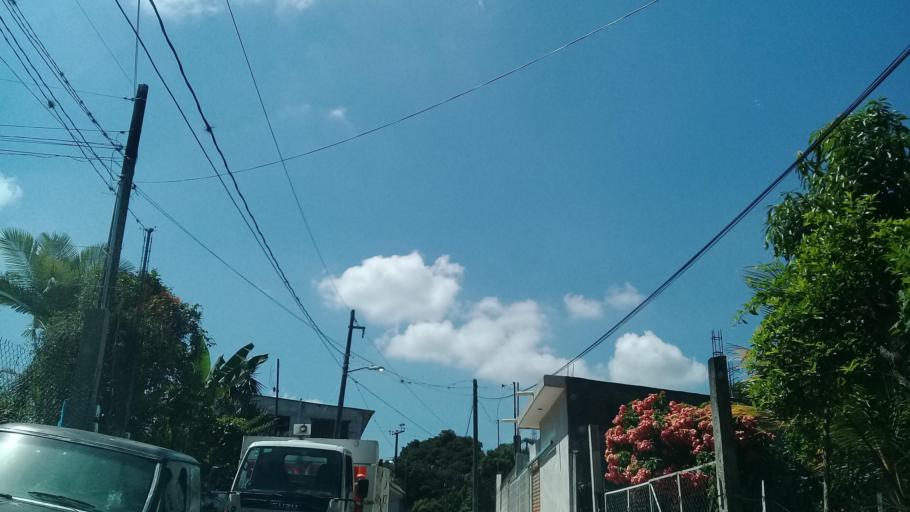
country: MX
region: Veracruz
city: Amatlan de los Reyes
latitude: 18.8416
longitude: -96.9162
